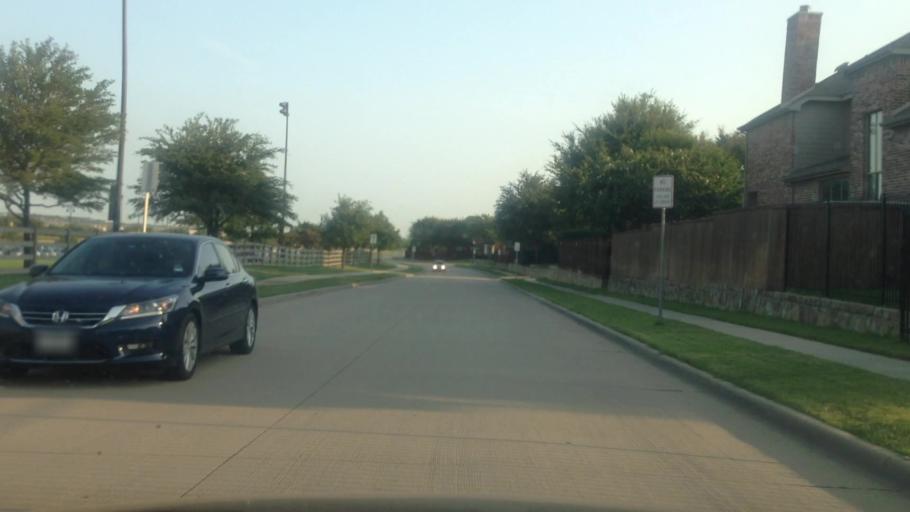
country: US
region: Texas
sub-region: Denton County
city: The Colony
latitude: 33.1288
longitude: -96.8648
